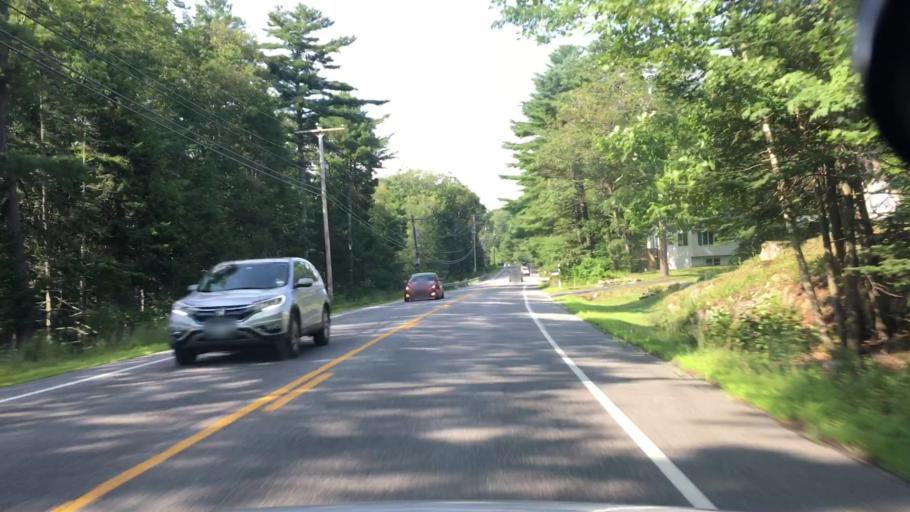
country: US
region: Maine
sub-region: Cumberland County
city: Harpswell Center
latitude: 43.8444
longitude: -69.9130
